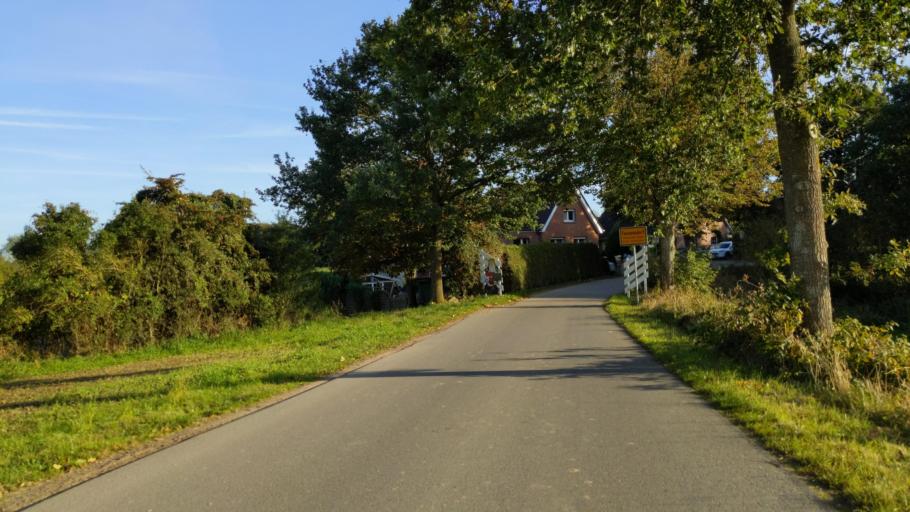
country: DE
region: Schleswig-Holstein
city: Eutin
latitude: 54.0933
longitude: 10.6504
